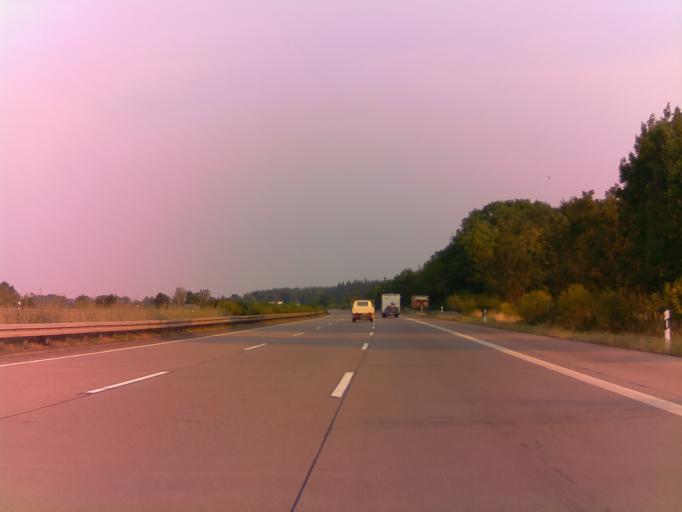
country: DE
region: Thuringia
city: Mechterstadt
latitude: 50.9313
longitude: 10.5050
